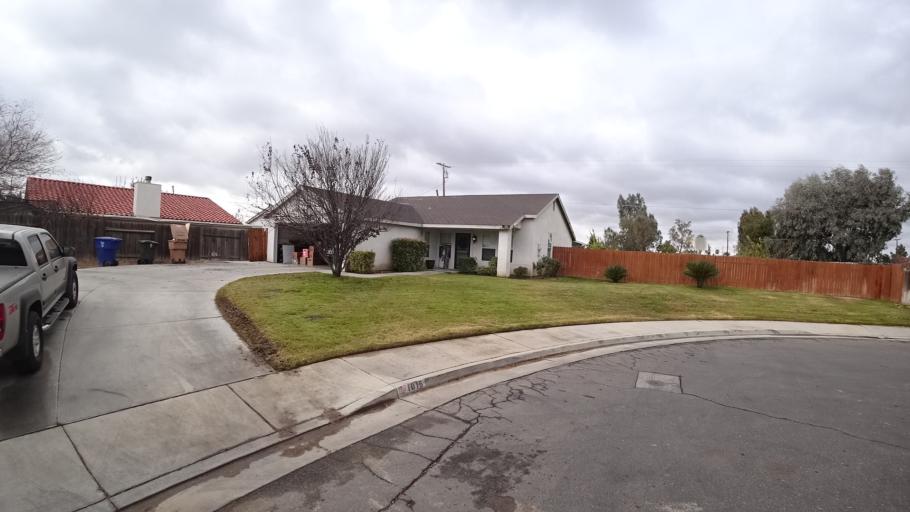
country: US
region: California
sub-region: Kern County
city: Greenfield
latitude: 35.2952
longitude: -119.0138
